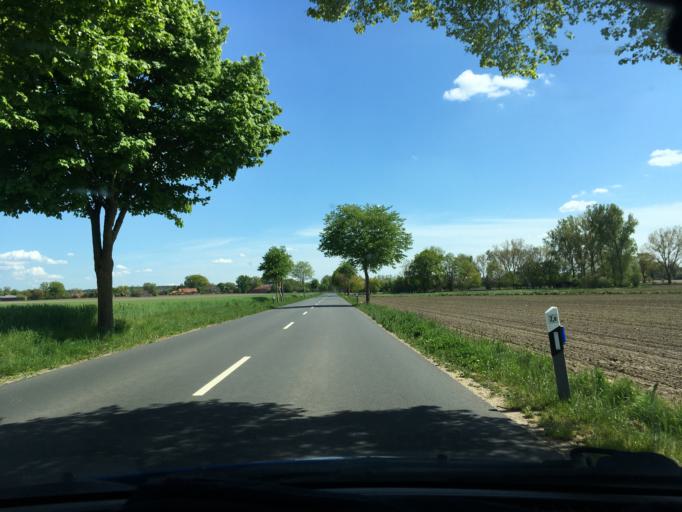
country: DE
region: Lower Saxony
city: Stoetze
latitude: 53.0767
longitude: 10.7631
